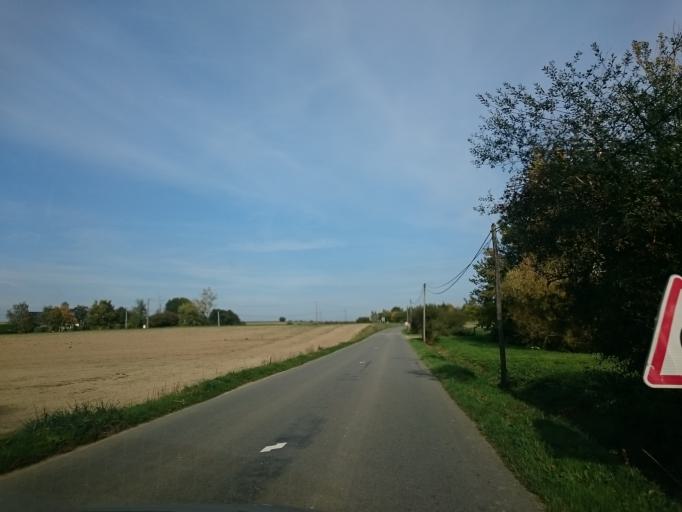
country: FR
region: Brittany
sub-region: Departement d'Ille-et-Vilaine
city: Corps-Nuds
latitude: 47.9503
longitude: -1.5560
